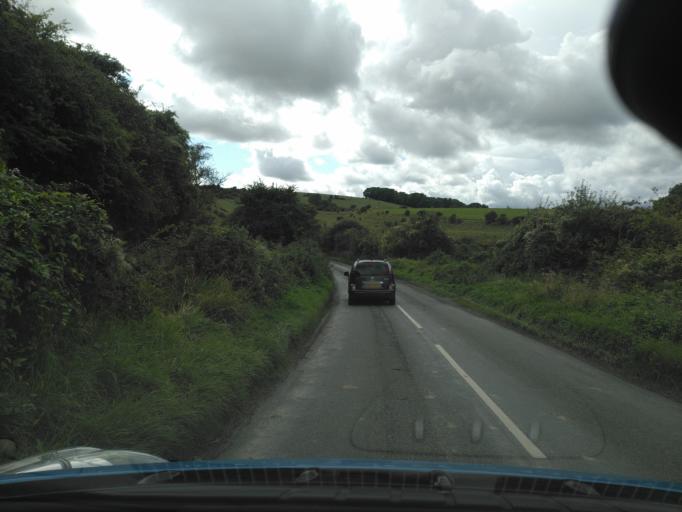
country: GB
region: England
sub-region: Oxfordshire
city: Stanford in the Vale
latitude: 51.5830
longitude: -1.5461
